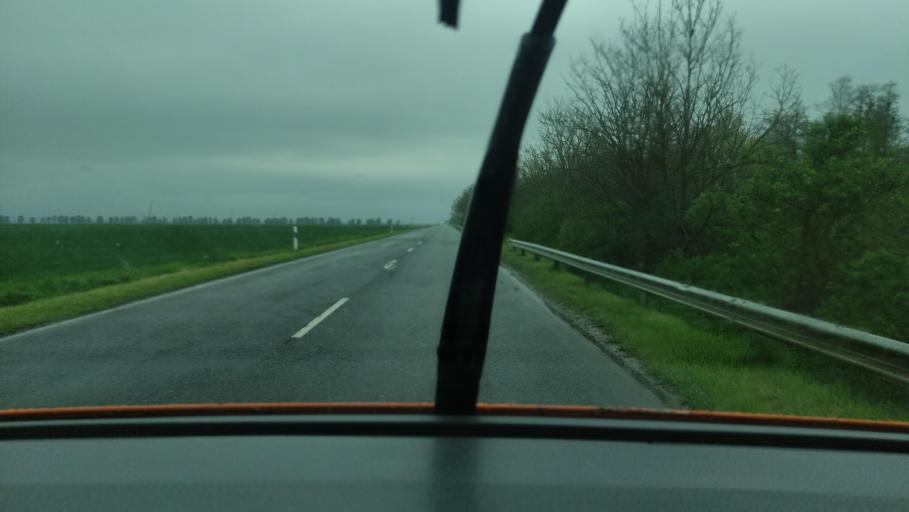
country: HU
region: Baranya
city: Mohacs
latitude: 45.9309
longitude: 18.6606
